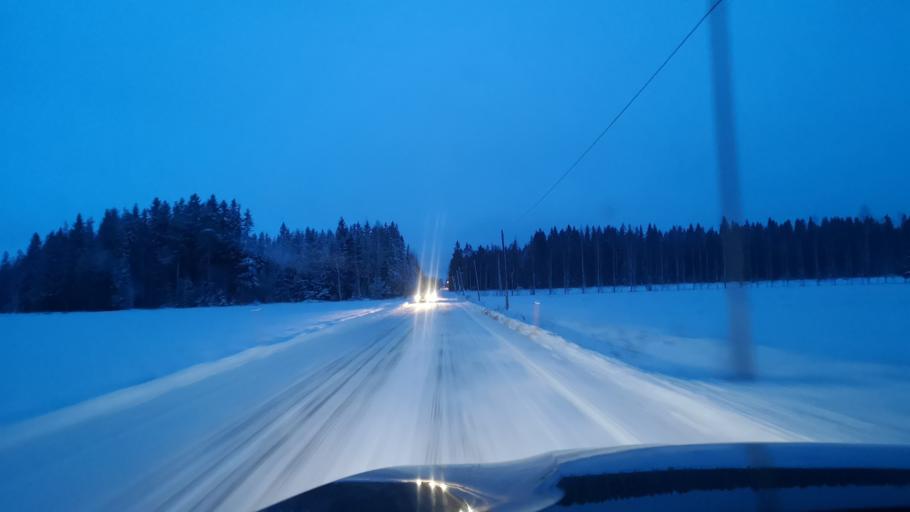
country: FI
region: Varsinais-Suomi
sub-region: Loimaa
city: Loimaa
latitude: 60.8754
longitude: 23.0897
